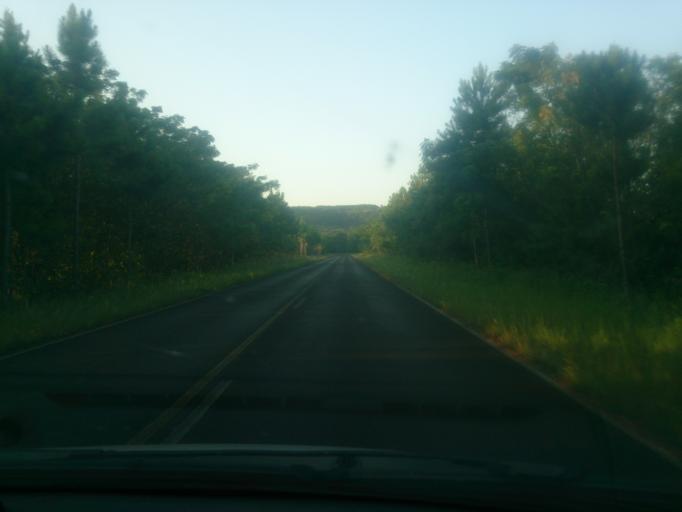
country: AR
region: Misiones
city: Panambi
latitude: -27.6711
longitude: -54.9124
